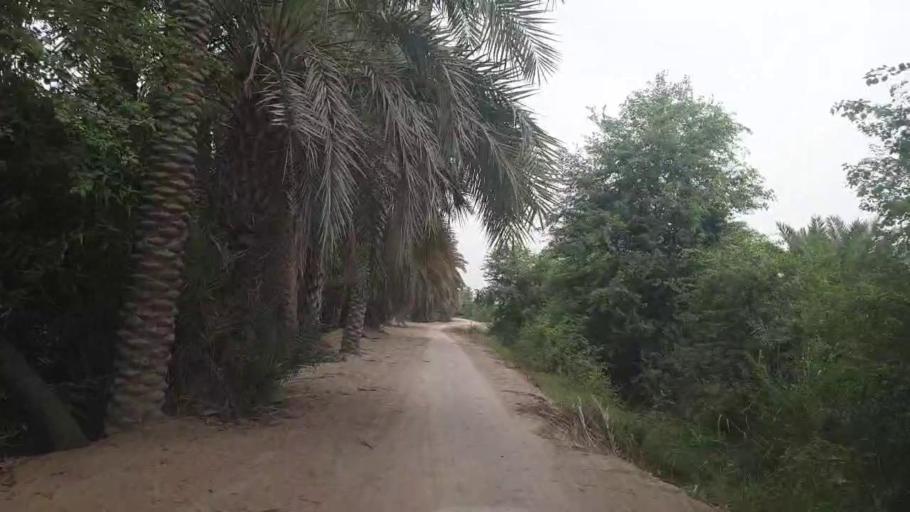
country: PK
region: Sindh
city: Khairpur
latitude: 27.5840
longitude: 68.7128
